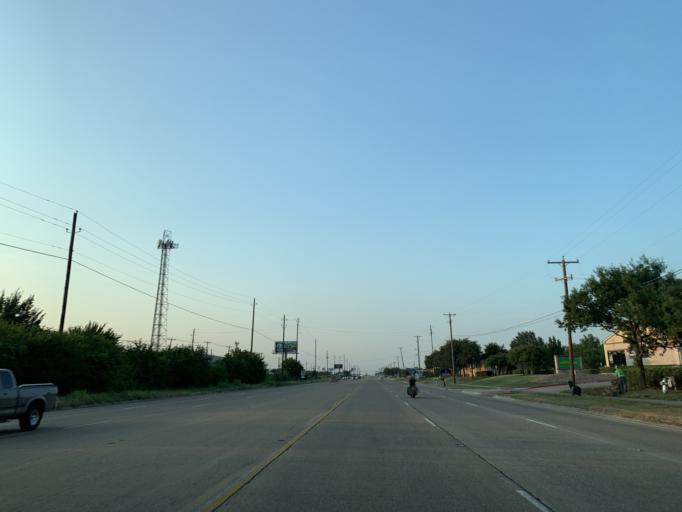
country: US
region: Texas
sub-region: Tarrant County
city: Keller
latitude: 32.9042
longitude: -97.2571
